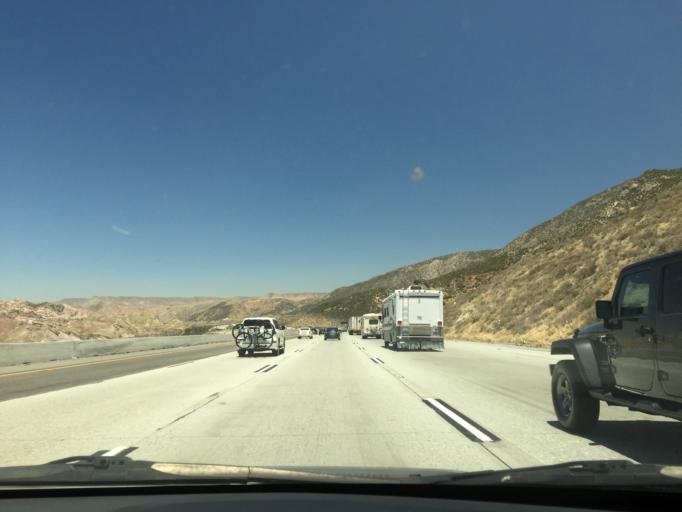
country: US
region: California
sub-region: San Bernardino County
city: Oak Hills
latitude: 34.2684
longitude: -117.4494
